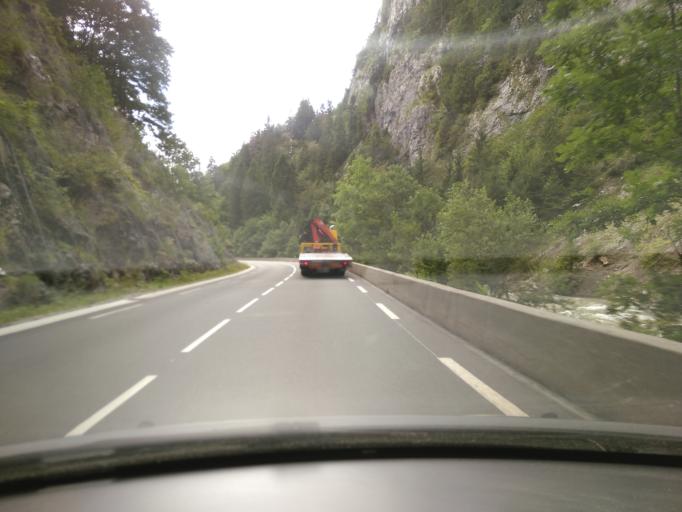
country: FR
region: Rhone-Alpes
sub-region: Departement de la Haute-Savoie
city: Saint-Jean-de-Sixt
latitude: 45.9339
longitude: 6.4008
